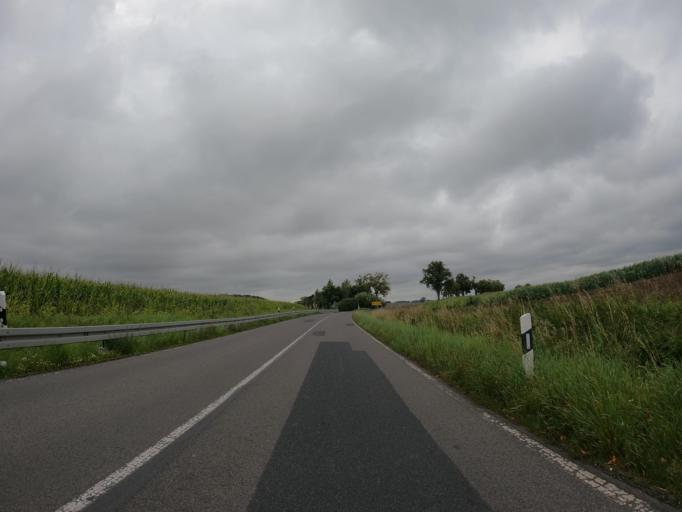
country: DE
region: Mecklenburg-Vorpommern
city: Garz
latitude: 54.3127
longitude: 13.3346
